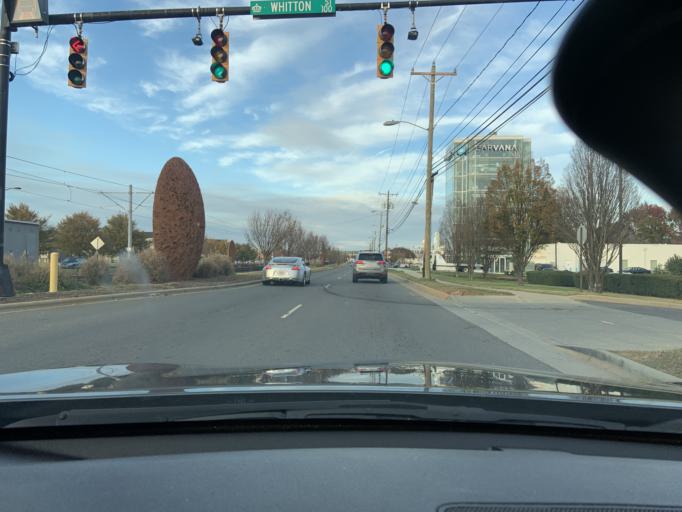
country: US
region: North Carolina
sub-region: Mecklenburg County
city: Charlotte
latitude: 35.1912
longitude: -80.8746
